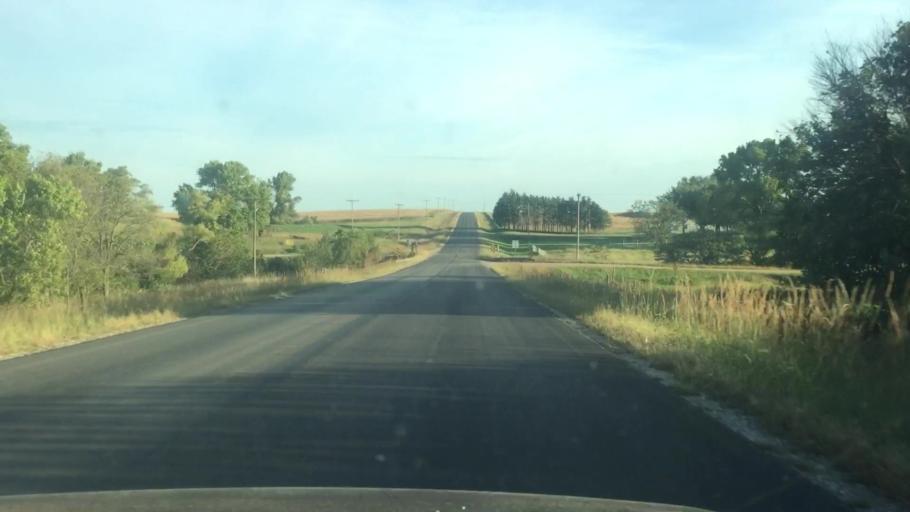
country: US
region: Kansas
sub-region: Marshall County
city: Marysville
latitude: 39.8991
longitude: -96.6010
